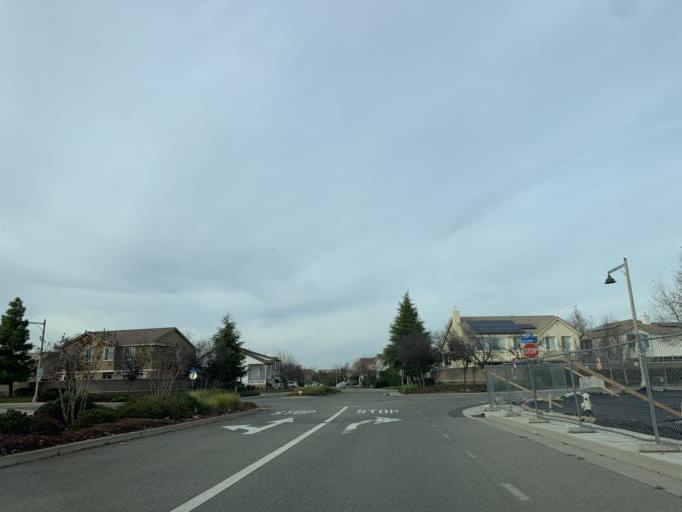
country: US
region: California
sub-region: Placer County
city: Lincoln
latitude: 38.8635
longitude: -121.3133
